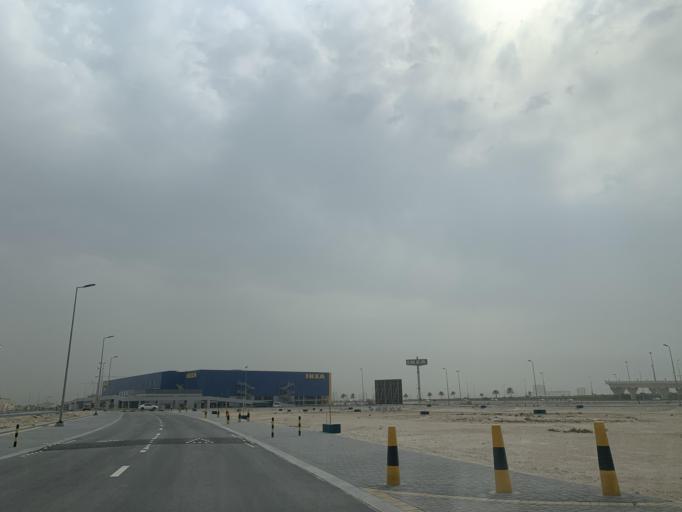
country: BH
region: Northern
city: Madinat `Isa
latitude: 26.1831
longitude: 50.5076
